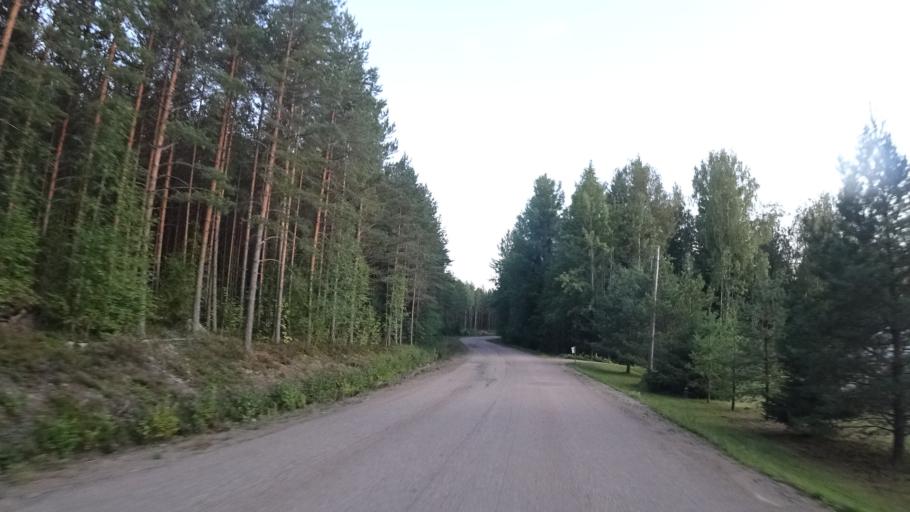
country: FI
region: Kymenlaakso
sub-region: Kotka-Hamina
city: Virojoki
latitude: 60.5919
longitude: 27.7630
